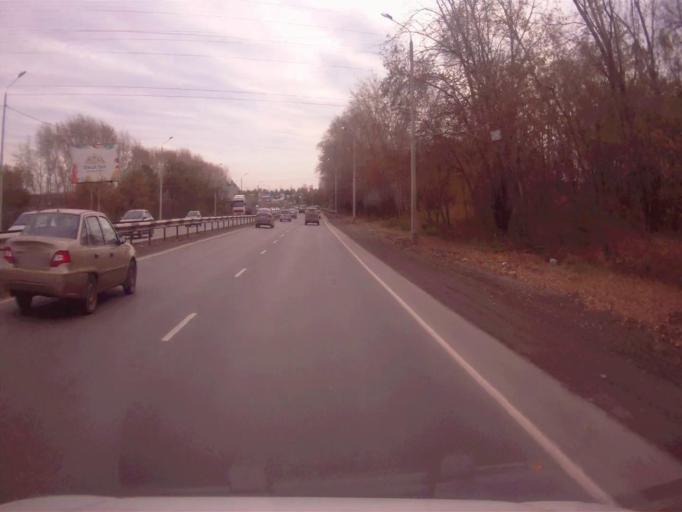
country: RU
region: Chelyabinsk
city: Novosineglazovskiy
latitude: 55.0504
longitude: 61.4131
